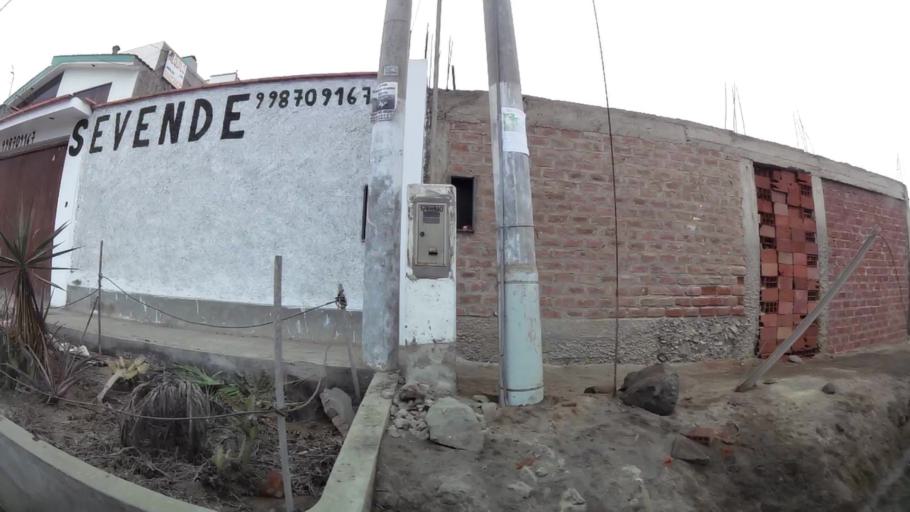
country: PE
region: Lima
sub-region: Lima
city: Punta Hermosa
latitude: -12.3330
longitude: -76.8288
